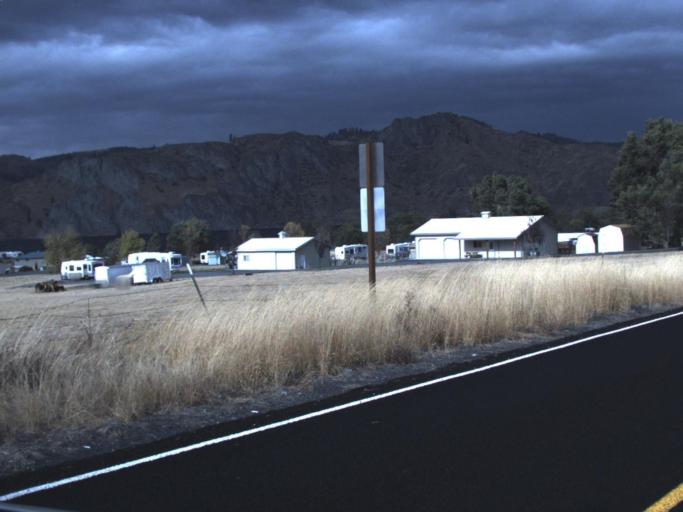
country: US
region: Washington
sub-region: Okanogan County
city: Coulee Dam
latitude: 47.9230
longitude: -118.6896
